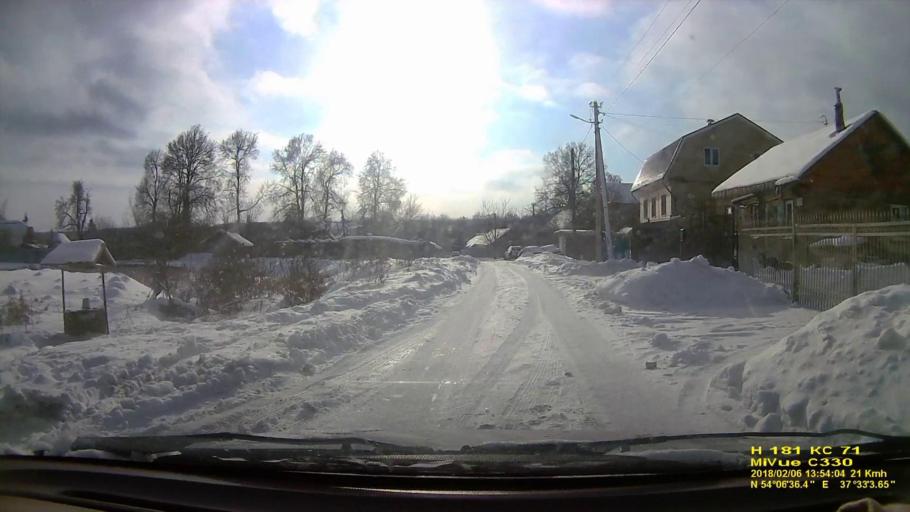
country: RU
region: Tula
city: Kosaya Gora
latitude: 54.1100
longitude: 37.5509
